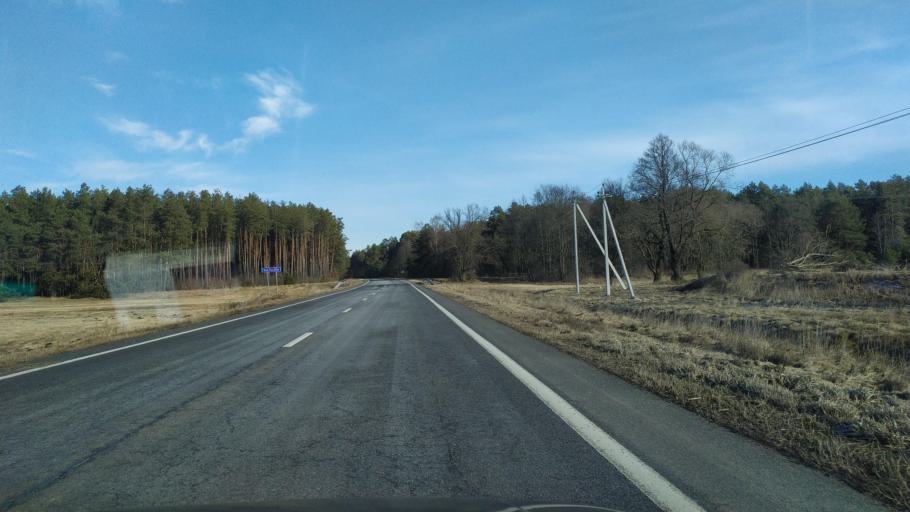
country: BY
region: Brest
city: Zhabinka
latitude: 52.4156
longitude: 24.1164
